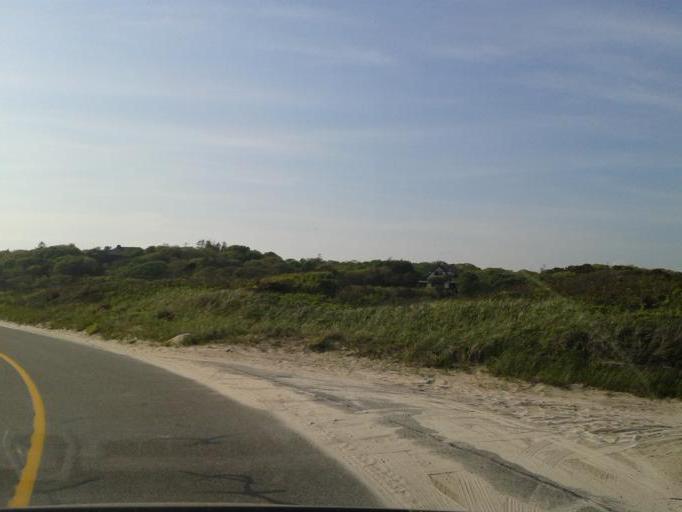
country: US
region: Massachusetts
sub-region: Barnstable County
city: Falmouth
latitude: 41.5169
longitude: -70.6575
